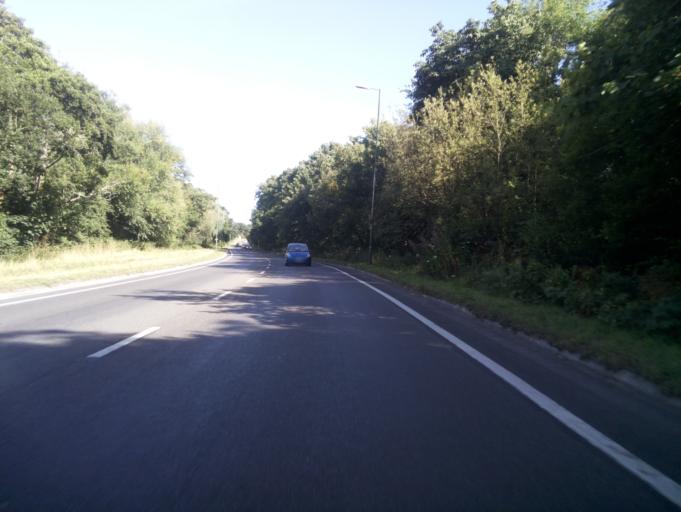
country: GB
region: England
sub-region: Bournemouth
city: Bournemouth
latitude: 50.7649
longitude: -1.8818
